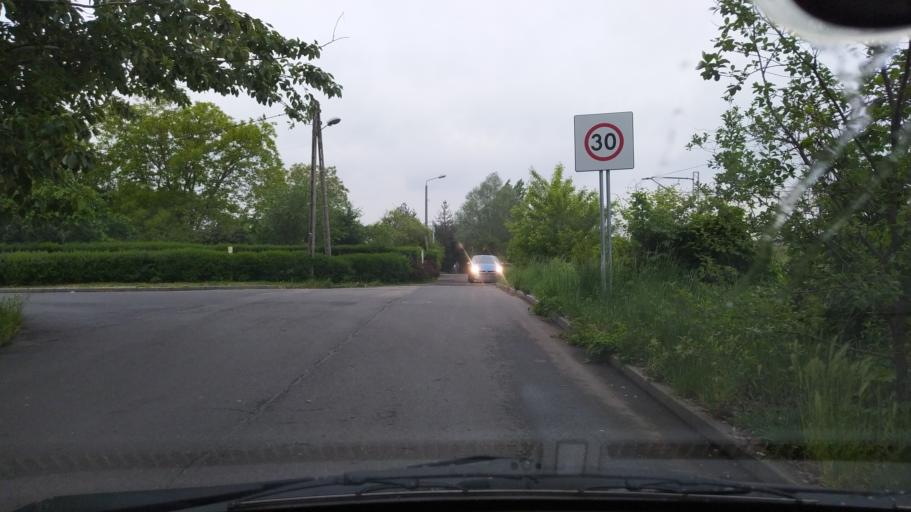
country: PL
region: Silesian Voivodeship
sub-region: Powiat gliwicki
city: Przyszowice
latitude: 50.2955
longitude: 18.7276
